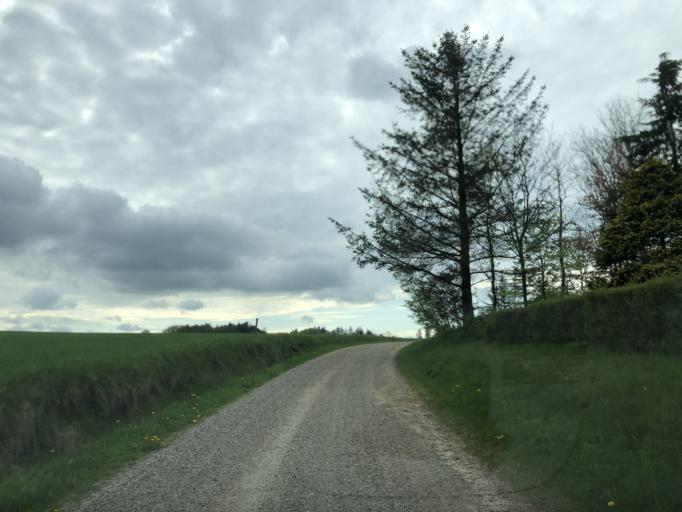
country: DK
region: Central Jutland
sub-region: Holstebro Kommune
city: Ulfborg
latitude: 56.1976
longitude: 8.4440
